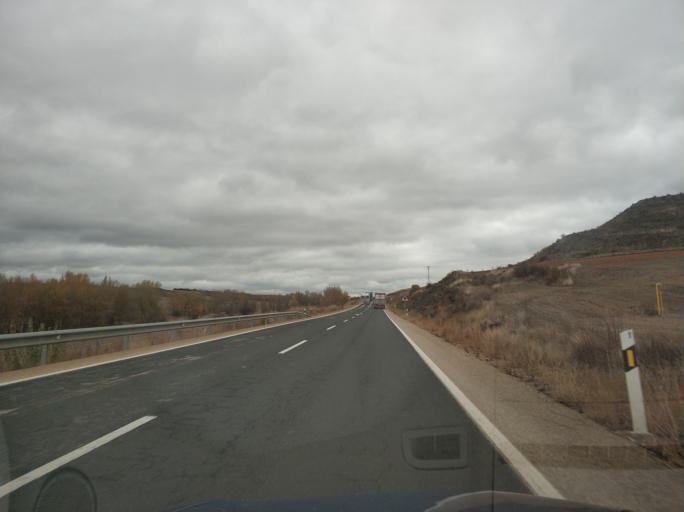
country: ES
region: Castille and Leon
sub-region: Provincia de Soria
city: San Esteban de Gormaz
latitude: 41.5802
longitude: -3.2157
